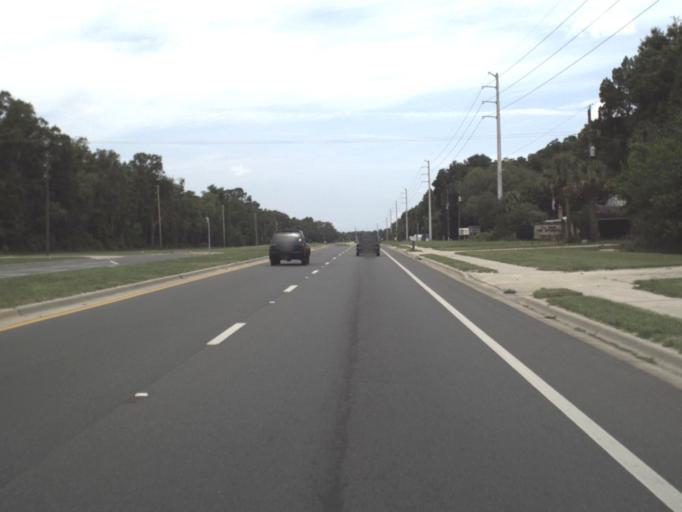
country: US
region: Florida
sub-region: Putnam County
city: Interlachen
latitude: 29.6275
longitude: -81.8650
